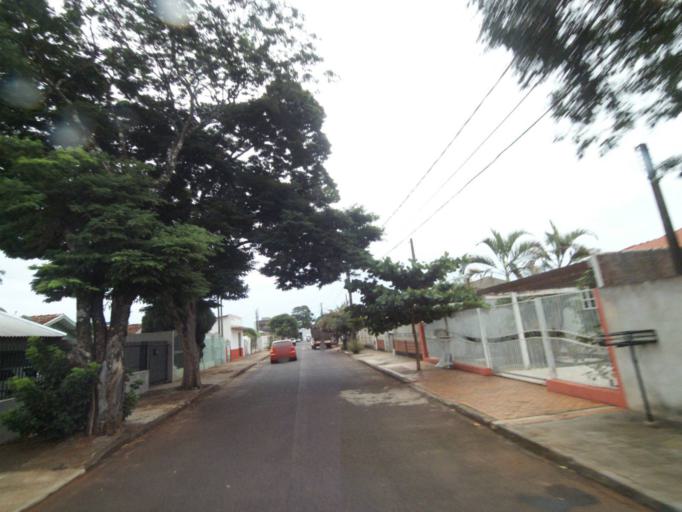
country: BR
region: Parana
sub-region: Campo Mourao
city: Campo Mourao
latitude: -24.0273
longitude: -52.3612
